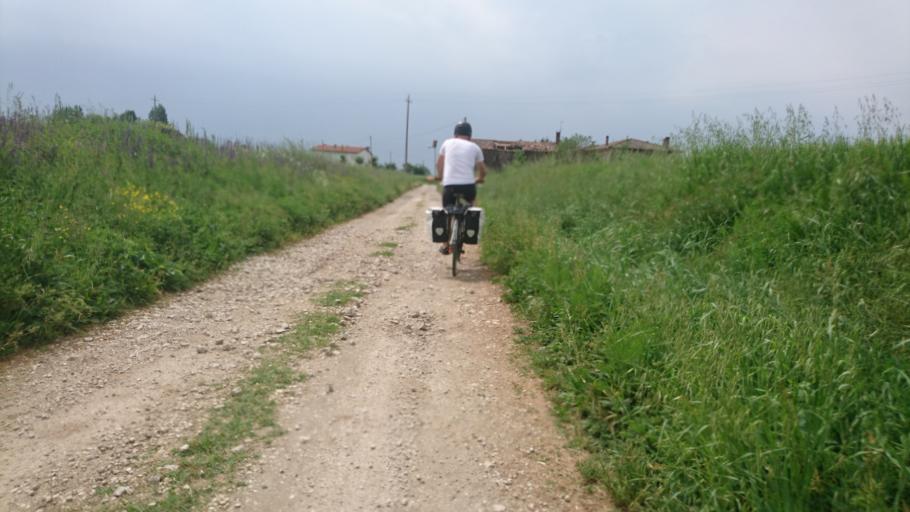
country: IT
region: Veneto
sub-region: Provincia di Padova
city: Monselice
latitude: 45.2181
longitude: 11.7311
